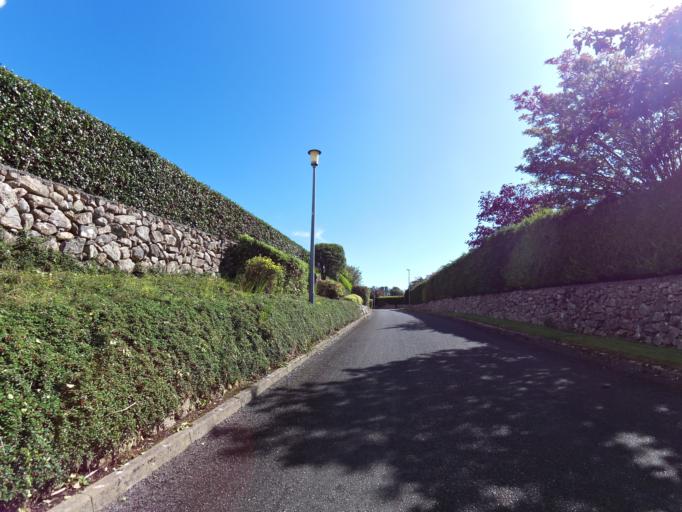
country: IE
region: Connaught
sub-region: County Galway
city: Gaillimh
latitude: 53.2879
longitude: -9.0847
